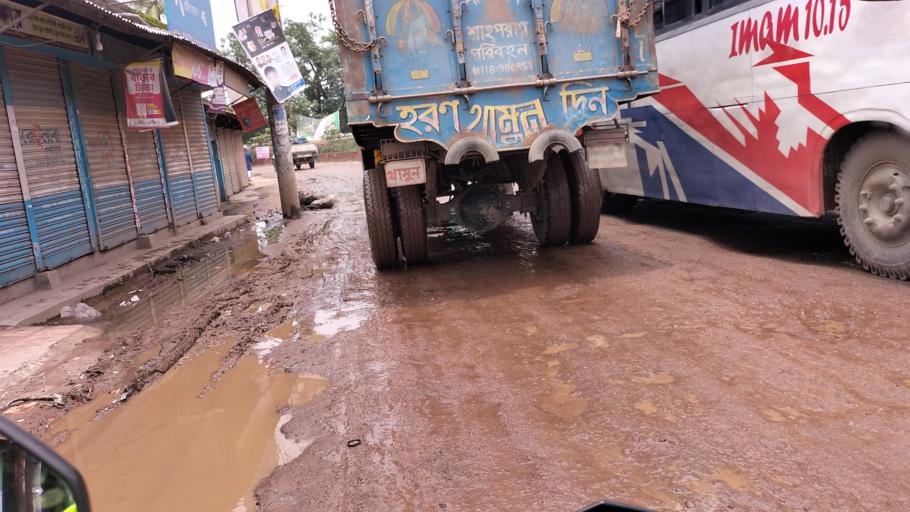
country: BD
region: Dhaka
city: Mymensingh
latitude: 24.7646
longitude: 90.4515
